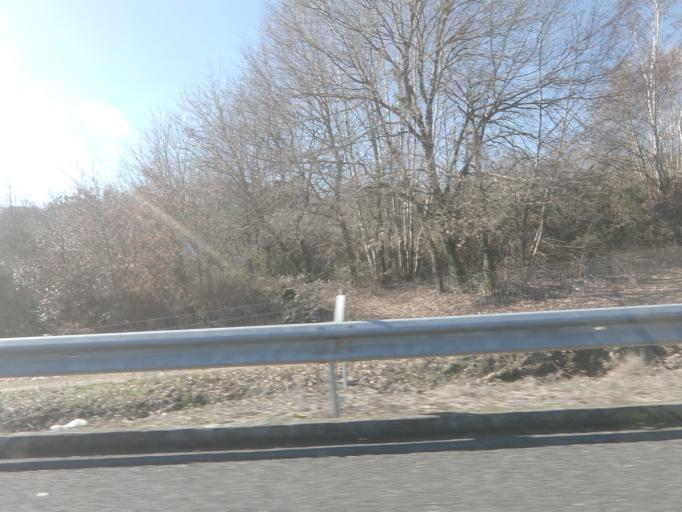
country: ES
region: Galicia
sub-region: Provincia de Pontevedra
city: Lalin
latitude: 42.6700
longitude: -8.1512
